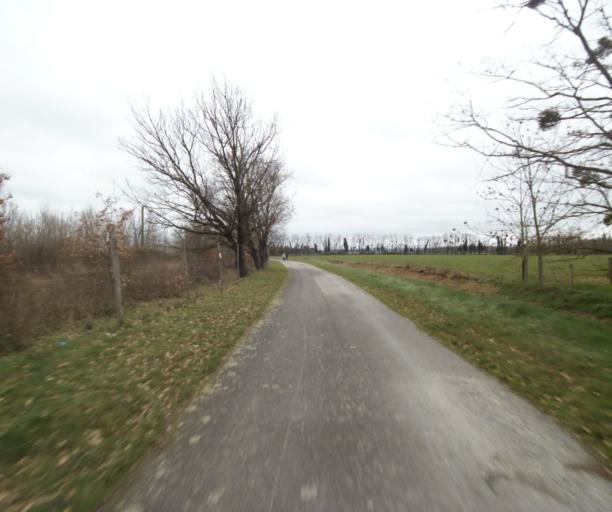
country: FR
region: Midi-Pyrenees
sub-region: Departement de l'Ariege
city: Saverdun
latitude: 43.2260
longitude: 1.6168
